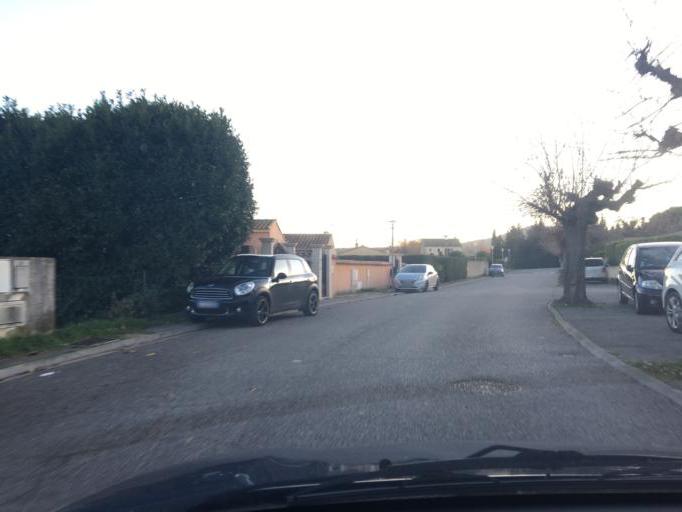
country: FR
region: Provence-Alpes-Cote d'Azur
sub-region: Departement des Bouches-du-Rhone
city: Mallemort
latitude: 43.7274
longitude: 5.1852
